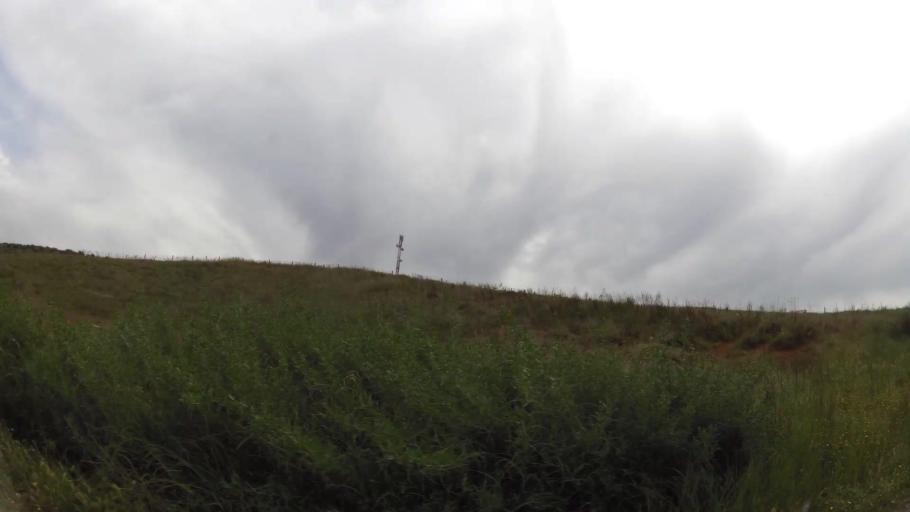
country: MA
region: Rabat-Sale-Zemmour-Zaer
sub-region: Khemisset
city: Khemisset
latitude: 33.7586
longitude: -6.2052
